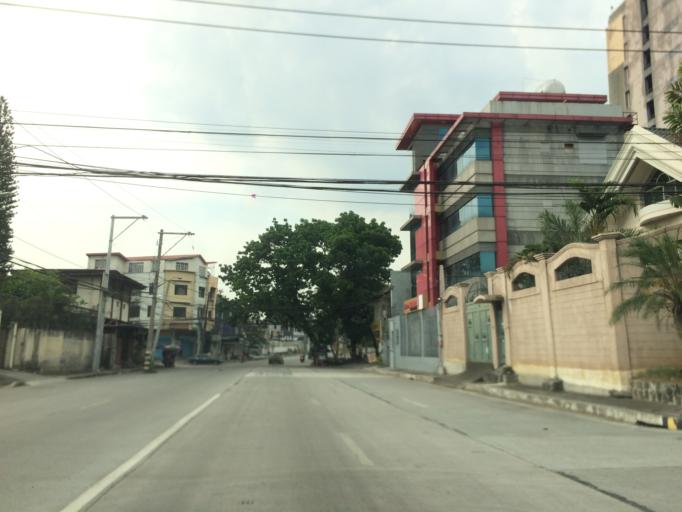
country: PH
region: Calabarzon
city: Del Monte
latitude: 14.6340
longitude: 121.0064
